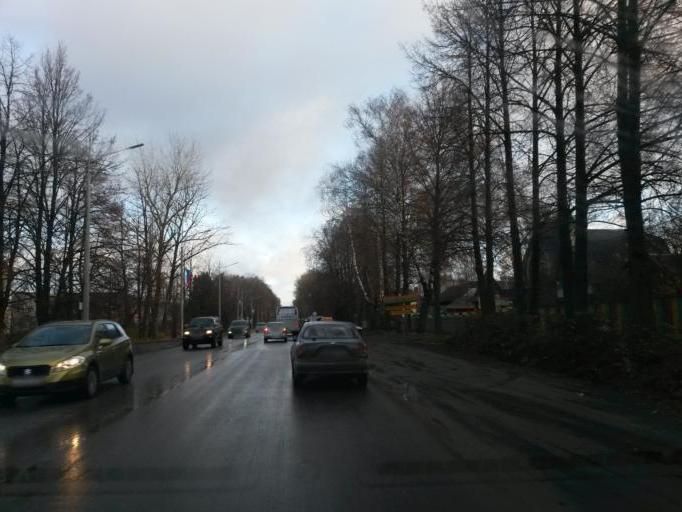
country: RU
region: Jaroslavl
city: Pereslavl'-Zalesskiy
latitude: 56.7483
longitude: 38.8600
